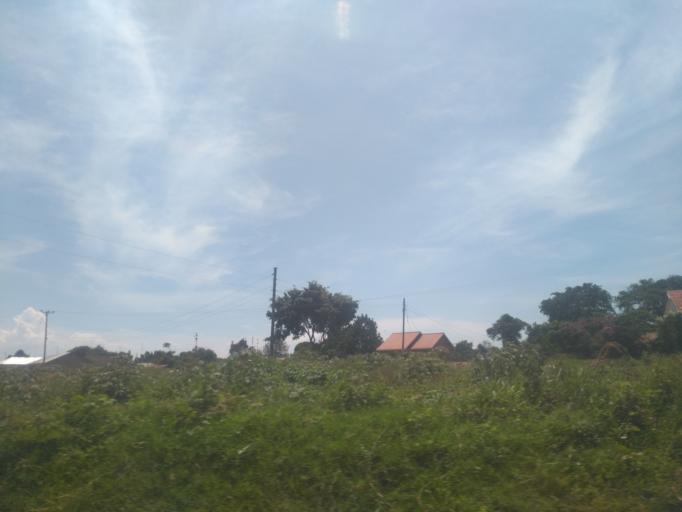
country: UG
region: Central Region
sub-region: Wakiso District
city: Entebbe
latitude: 0.0349
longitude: 32.4343
